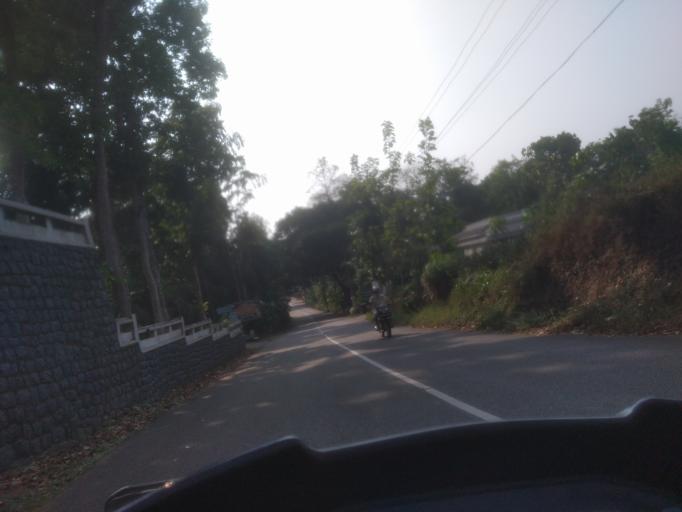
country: IN
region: Kerala
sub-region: Ernakulam
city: Piravam
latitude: 9.8628
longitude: 76.5295
